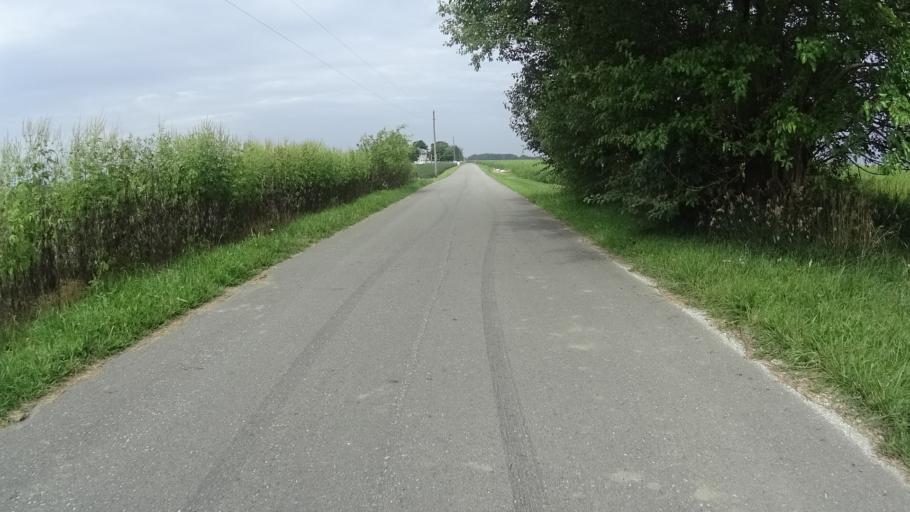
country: US
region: Indiana
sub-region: Madison County
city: Ingalls
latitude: 40.0073
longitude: -85.8026
